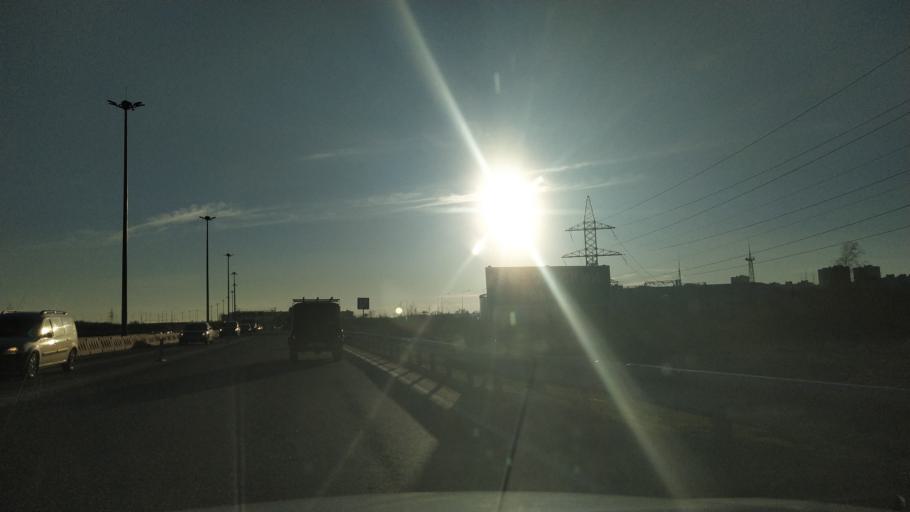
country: RU
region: St.-Petersburg
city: Pargolovo
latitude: 60.0993
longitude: 30.2826
